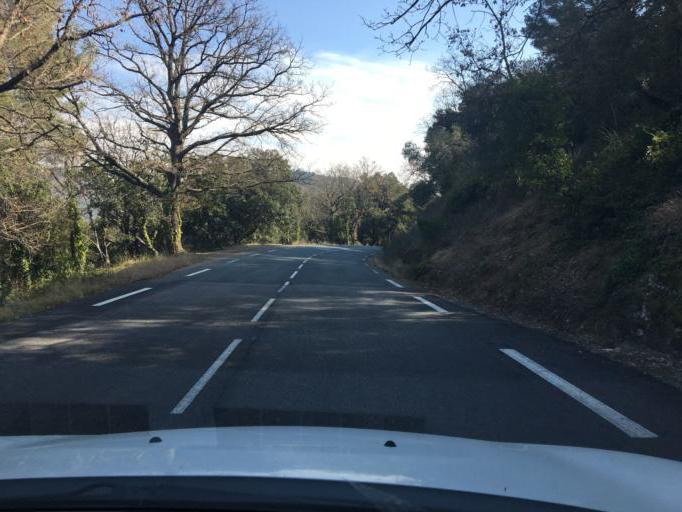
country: FR
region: Provence-Alpes-Cote d'Azur
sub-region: Departement du Var
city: Bargemon
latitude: 43.6127
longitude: 6.5467
